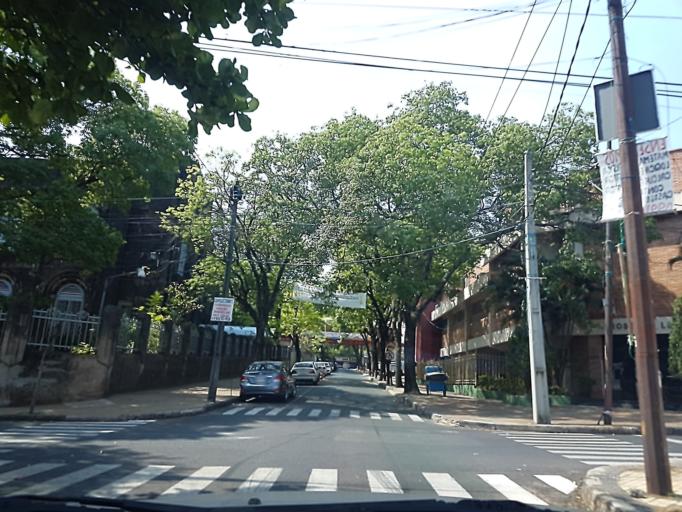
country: PY
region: Asuncion
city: Asuncion
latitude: -25.2898
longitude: -57.6168
